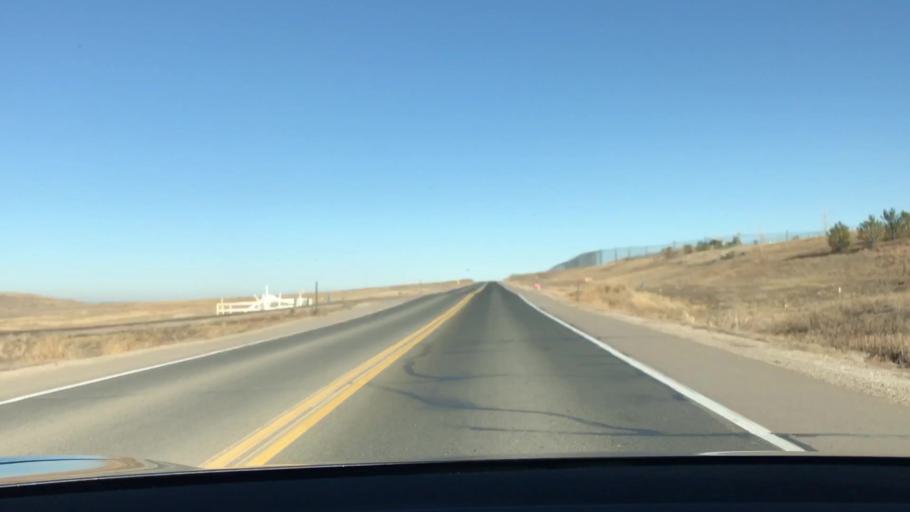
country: US
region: Colorado
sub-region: Boulder County
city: Erie
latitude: 40.0176
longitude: -105.0183
